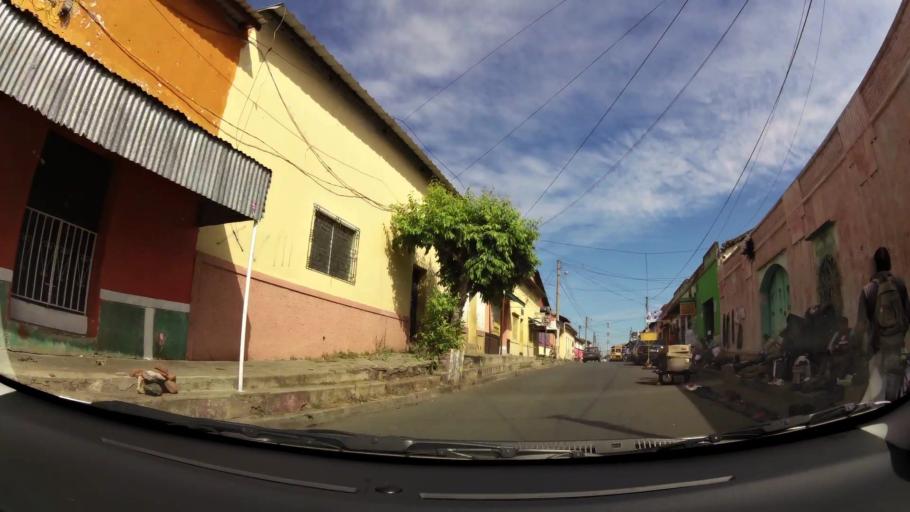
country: SV
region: Santa Ana
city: Chalchuapa
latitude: 13.9863
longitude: -89.6788
